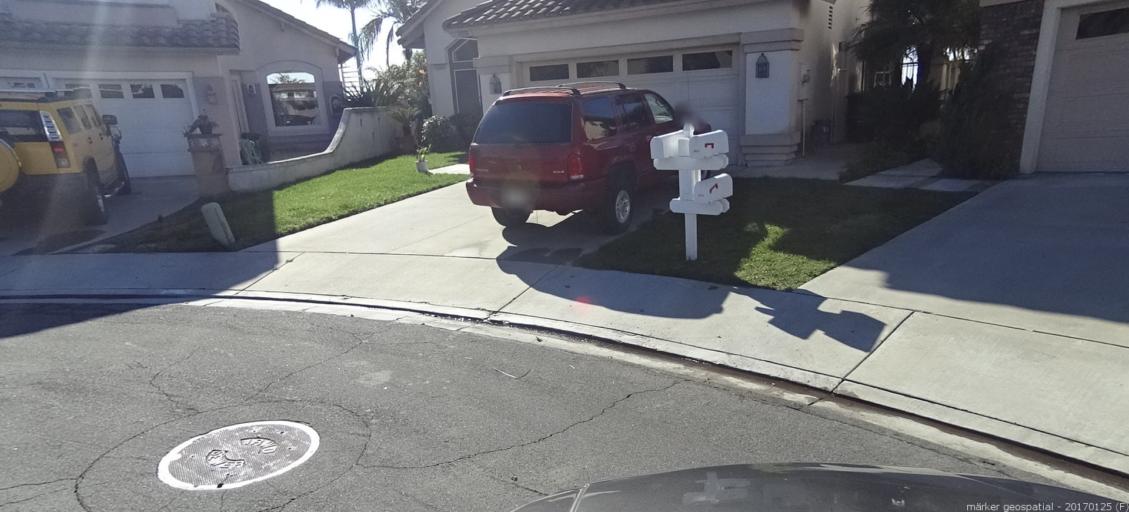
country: US
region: California
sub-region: Orange County
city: Portola Hills
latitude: 33.6814
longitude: -117.6329
